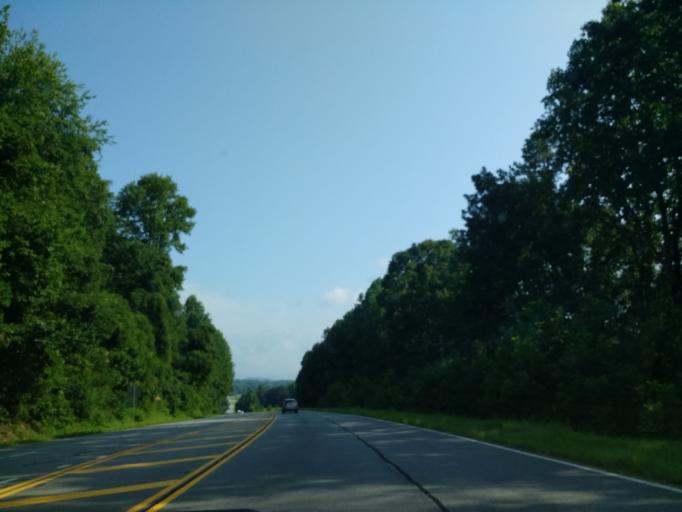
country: US
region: Georgia
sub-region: White County
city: Cleveland
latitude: 34.5253
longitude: -83.7547
